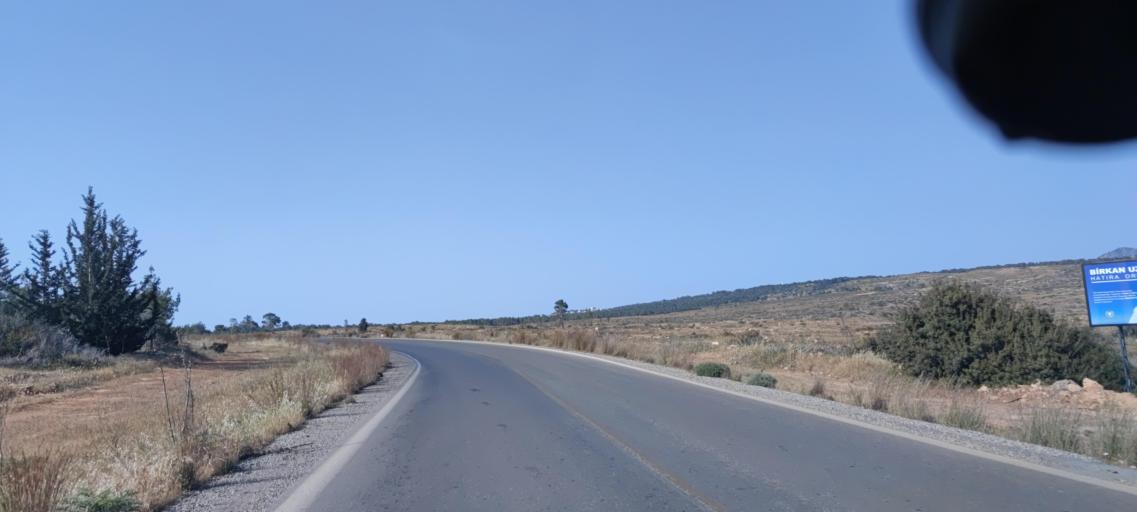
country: CY
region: Lefkosia
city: Morfou
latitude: 35.2768
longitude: 33.0413
